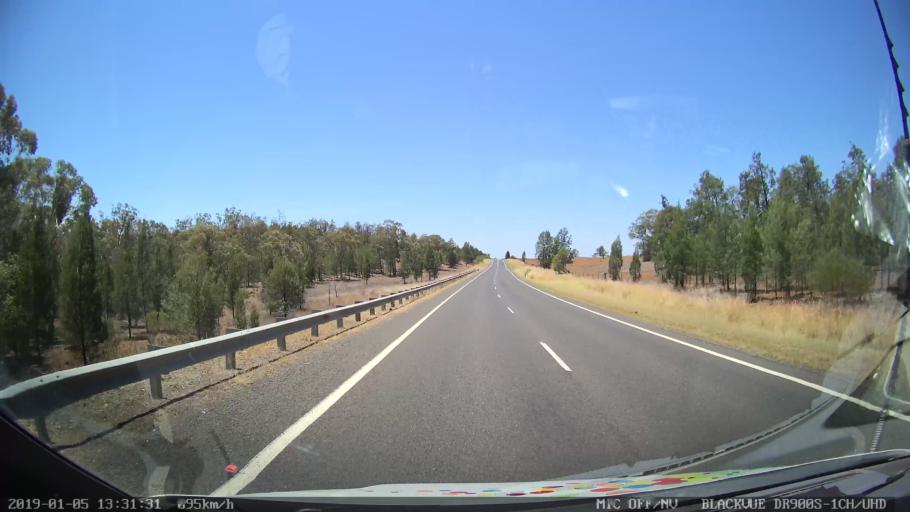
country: AU
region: New South Wales
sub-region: Gunnedah
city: Gunnedah
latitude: -31.0103
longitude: 150.0853
